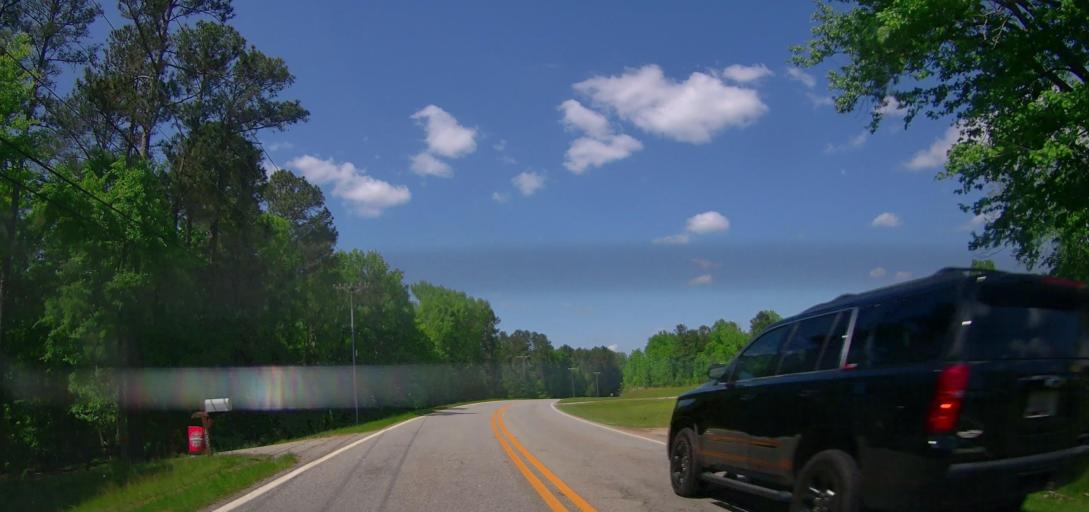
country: US
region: Georgia
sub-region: Putnam County
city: Eatonton
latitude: 33.2820
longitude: -83.3042
